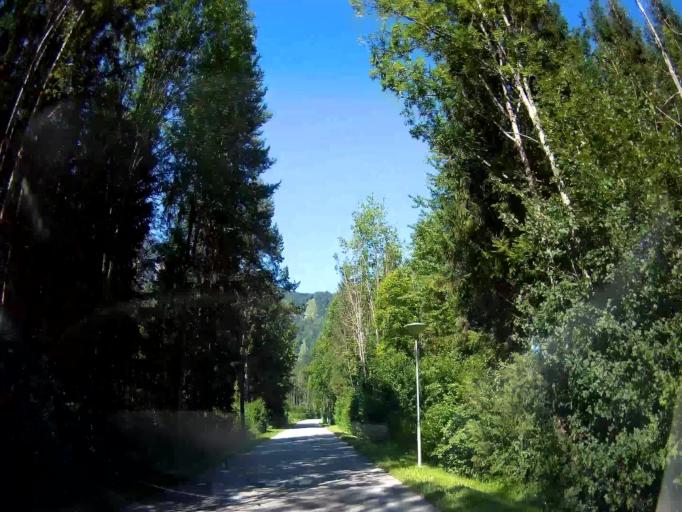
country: AT
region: Carinthia
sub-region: Politischer Bezirk Klagenfurt Land
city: Ferlach
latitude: 46.5234
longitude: 14.2879
